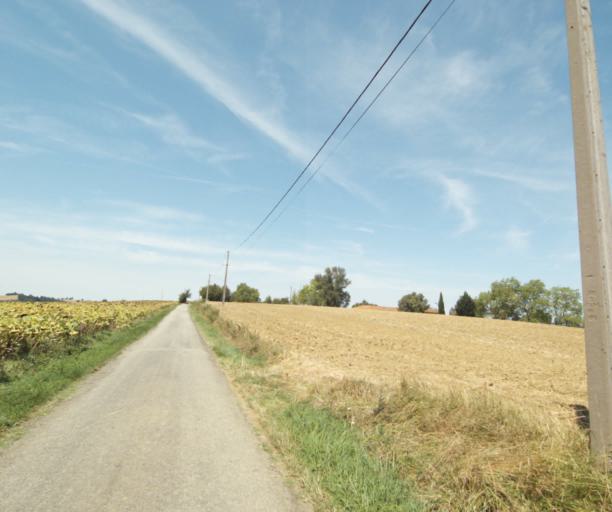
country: FR
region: Midi-Pyrenees
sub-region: Departement de l'Ariege
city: Lezat-sur-Leze
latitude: 43.2873
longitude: 1.3022
